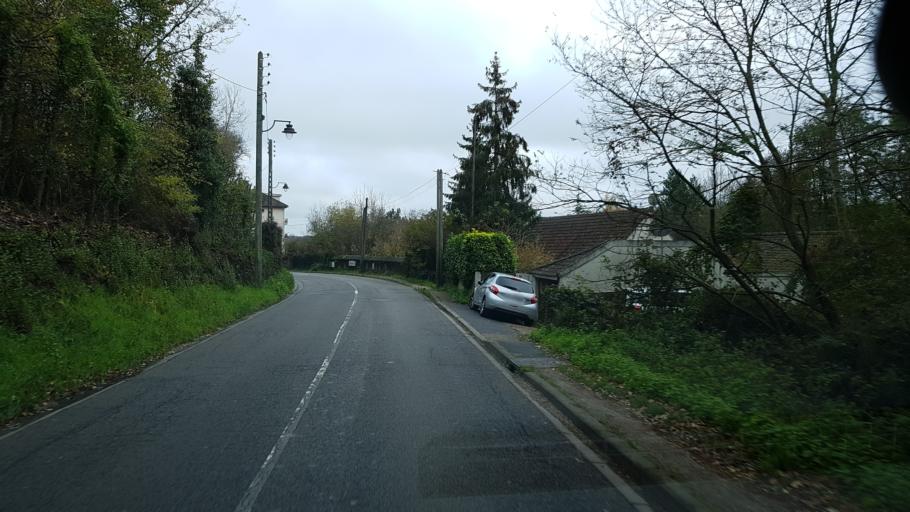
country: FR
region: Ile-de-France
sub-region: Departement des Yvelines
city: Chevreuse
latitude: 48.7108
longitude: 2.0348
